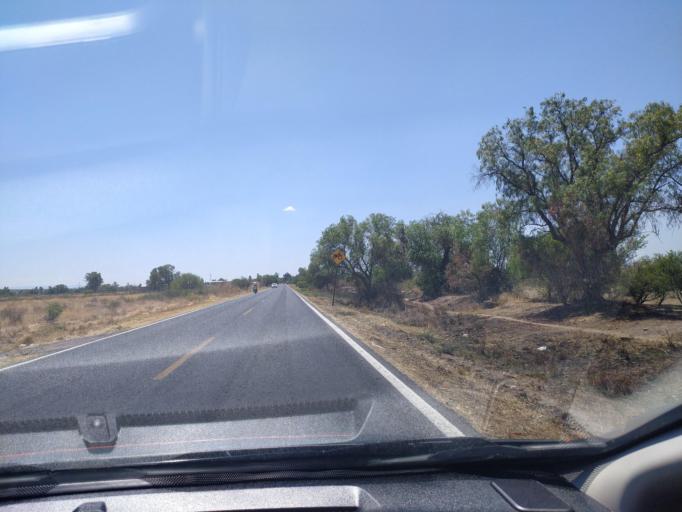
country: MX
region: Guanajuato
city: San Roque
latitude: 20.9528
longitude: -101.8515
